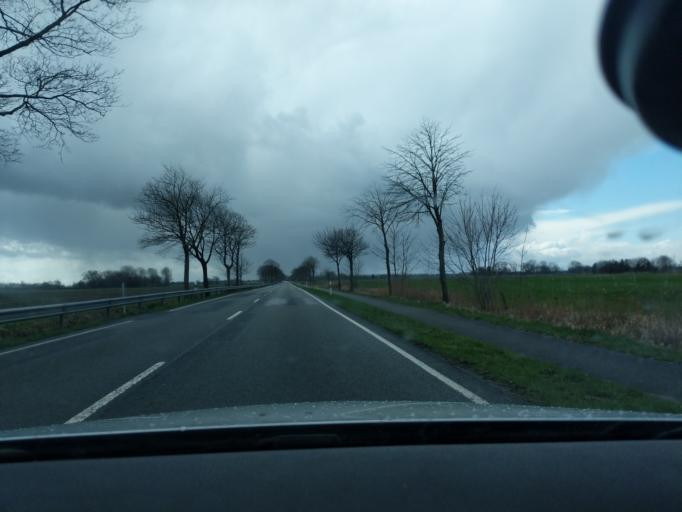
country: DE
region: Lower Saxony
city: Osten
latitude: 53.7172
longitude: 9.2317
